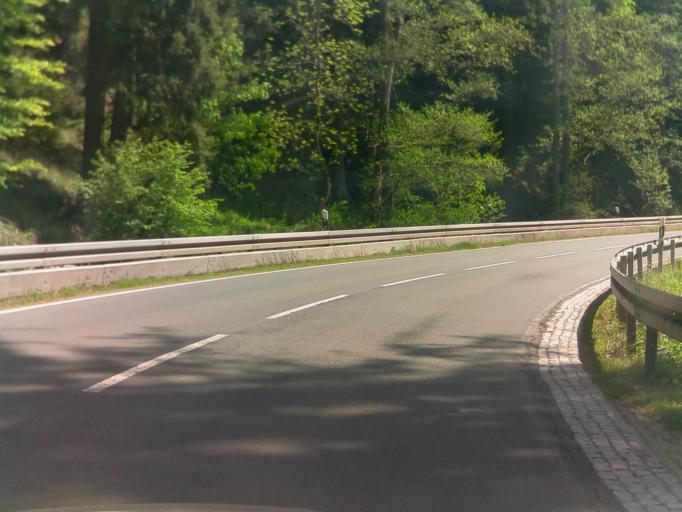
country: DE
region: Saxony-Anhalt
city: Hasselfelde
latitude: 51.6391
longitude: 10.8148
